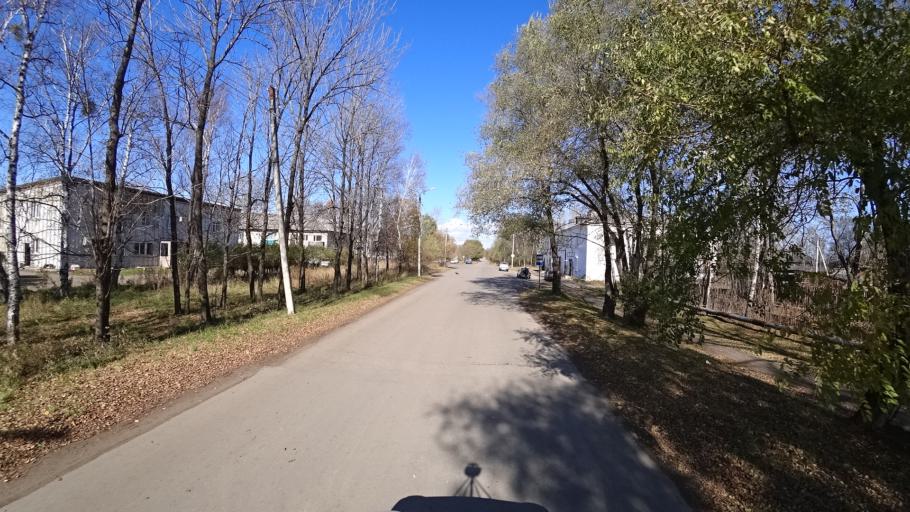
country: RU
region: Khabarovsk Krai
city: Amursk
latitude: 50.0985
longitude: 136.4976
